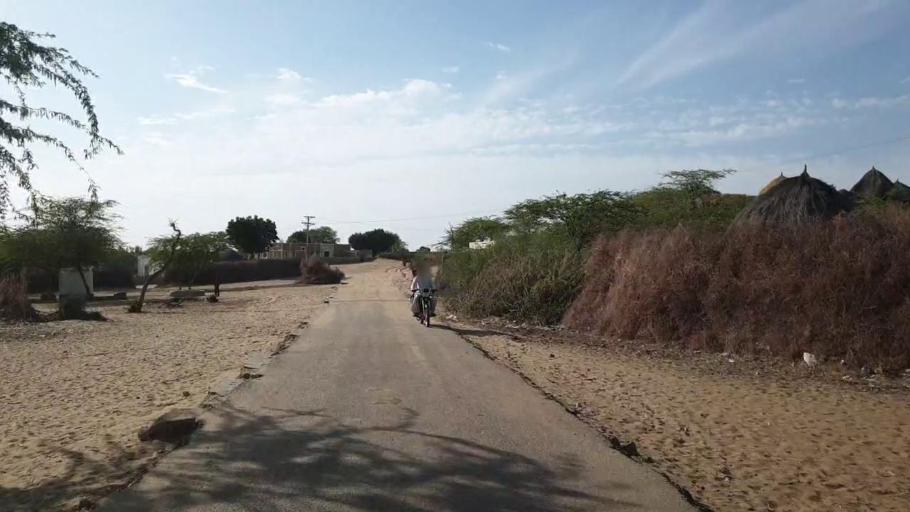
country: PK
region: Sindh
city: Nabisar
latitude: 25.0445
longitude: 70.0136
